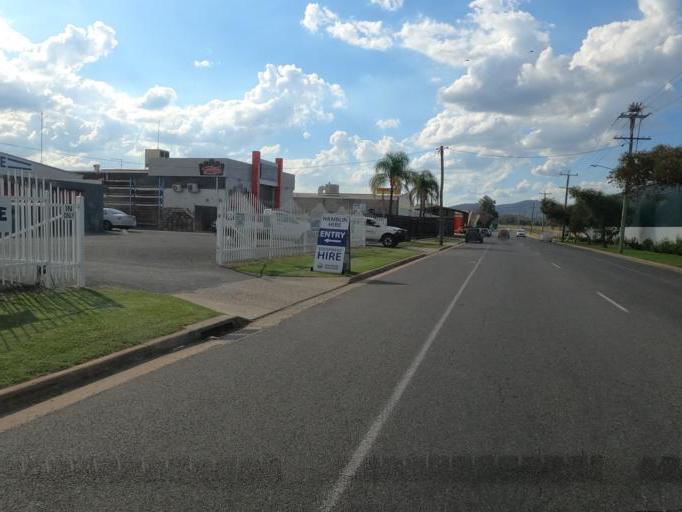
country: AU
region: New South Wales
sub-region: Albury Municipality
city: East Albury
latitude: -36.0738
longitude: 146.9478
